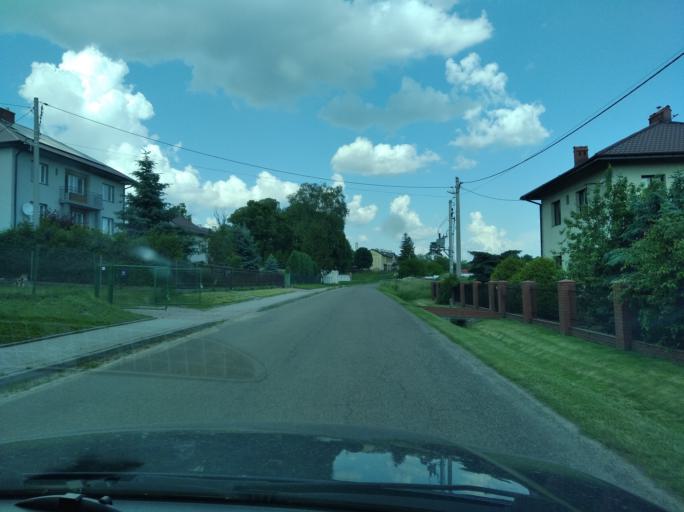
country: PL
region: Subcarpathian Voivodeship
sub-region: Powiat jaroslawski
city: Ostrow
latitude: 49.9390
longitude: 22.7230
